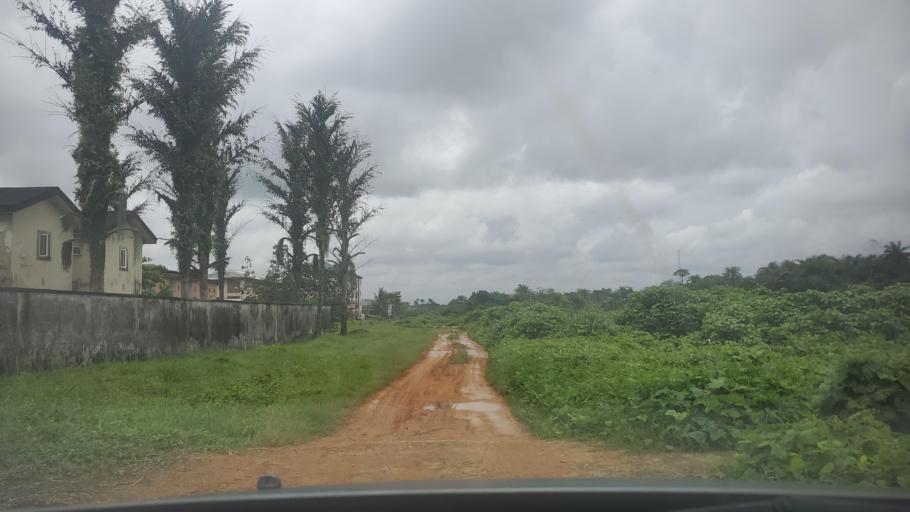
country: NG
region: Rivers
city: Emuoha
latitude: 4.8990
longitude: 6.9214
